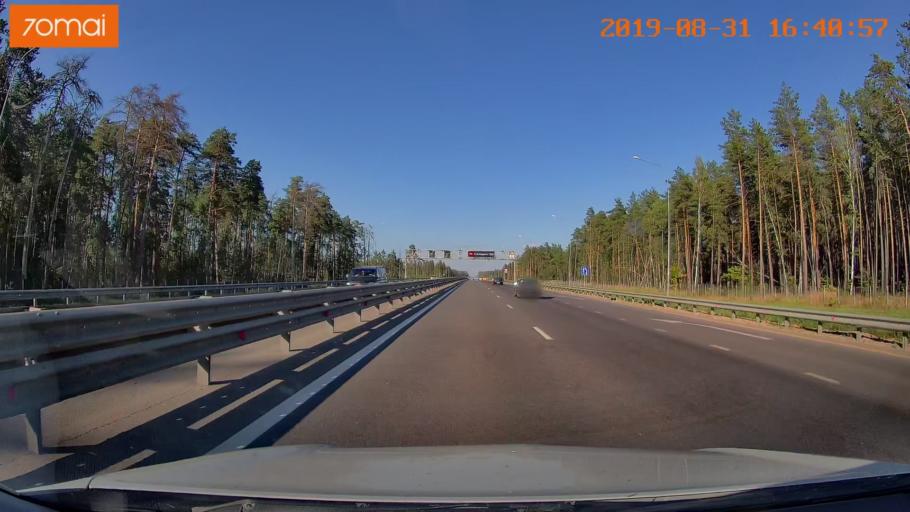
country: RU
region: Kaluga
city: Kurovskoye
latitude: 54.5731
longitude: 36.0584
